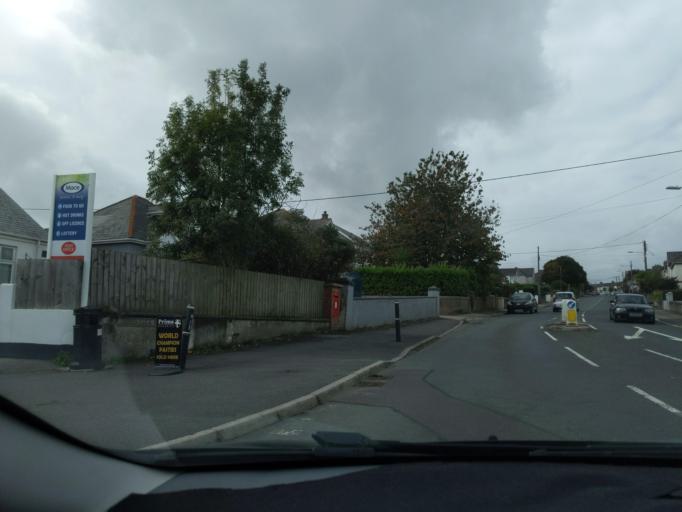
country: GB
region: England
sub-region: Cornwall
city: Par
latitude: 50.3501
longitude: -4.7219
